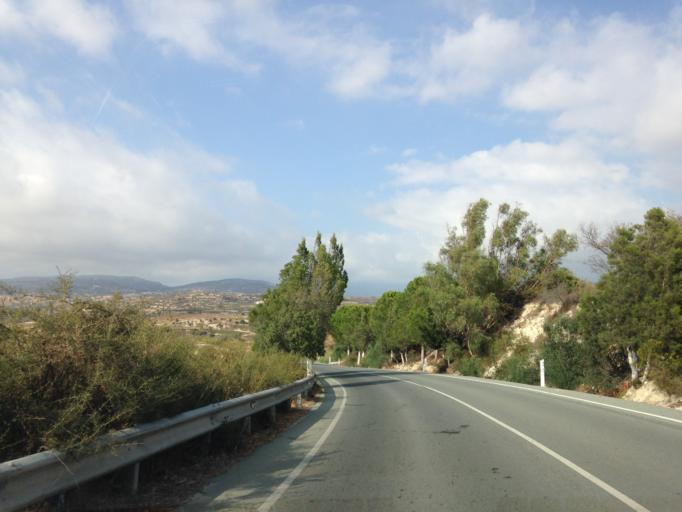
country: CY
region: Limassol
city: Pachna
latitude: 34.7898
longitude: 32.7989
